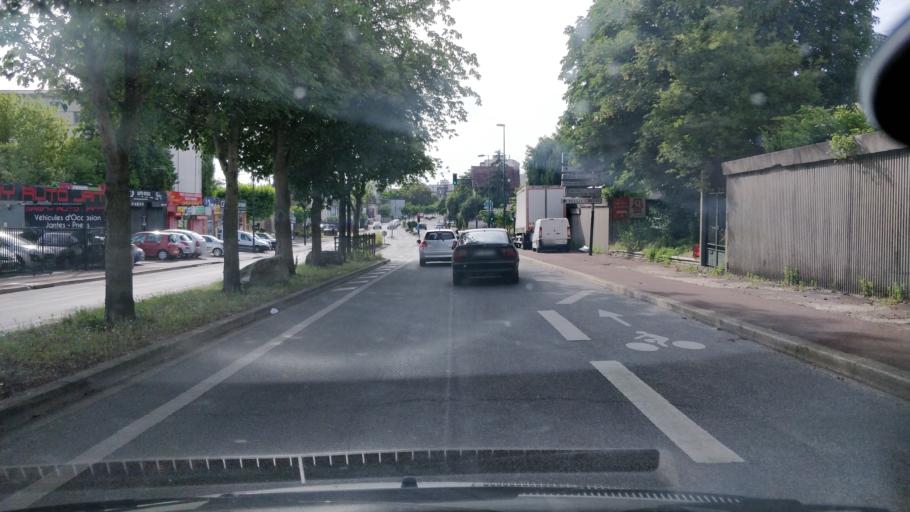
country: FR
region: Ile-de-France
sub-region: Departement de Seine-Saint-Denis
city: Gagny
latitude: 48.8825
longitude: 2.5363
